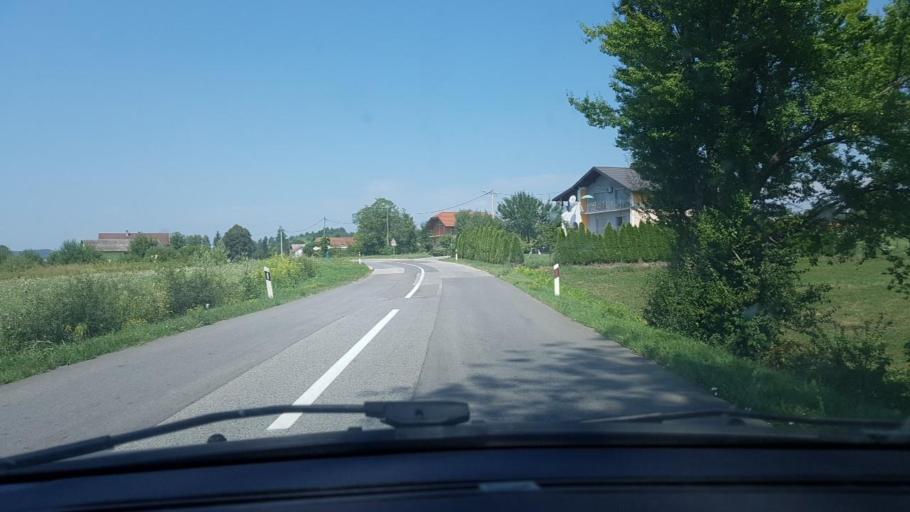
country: BA
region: Federation of Bosnia and Herzegovina
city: Velika Kladusa
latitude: 45.2152
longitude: 15.7603
